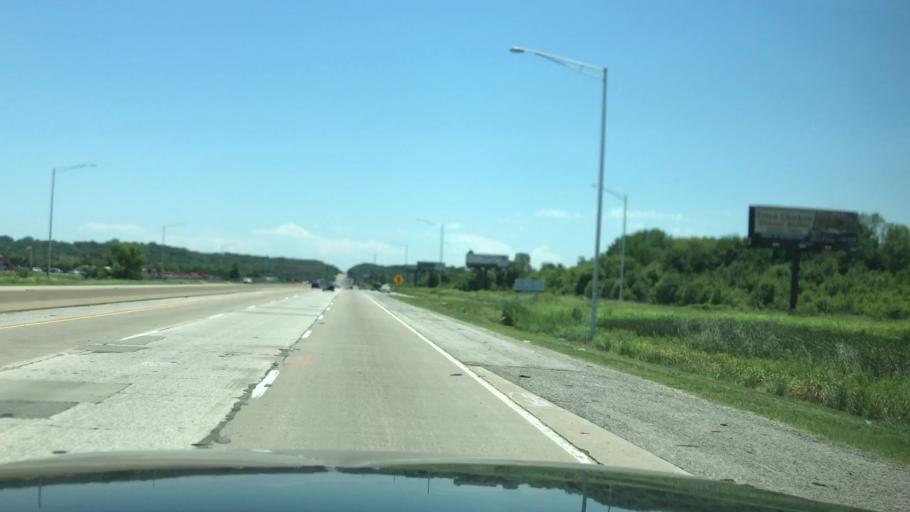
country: US
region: Illinois
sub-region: Saint Clair County
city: Alorton
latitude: 38.5812
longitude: -90.1066
